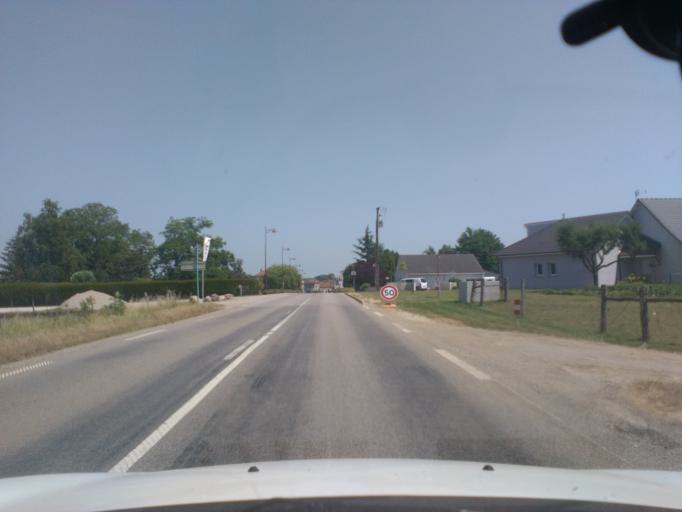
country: FR
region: Lorraine
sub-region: Departement des Vosges
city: Vittel
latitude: 48.3087
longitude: 5.9685
